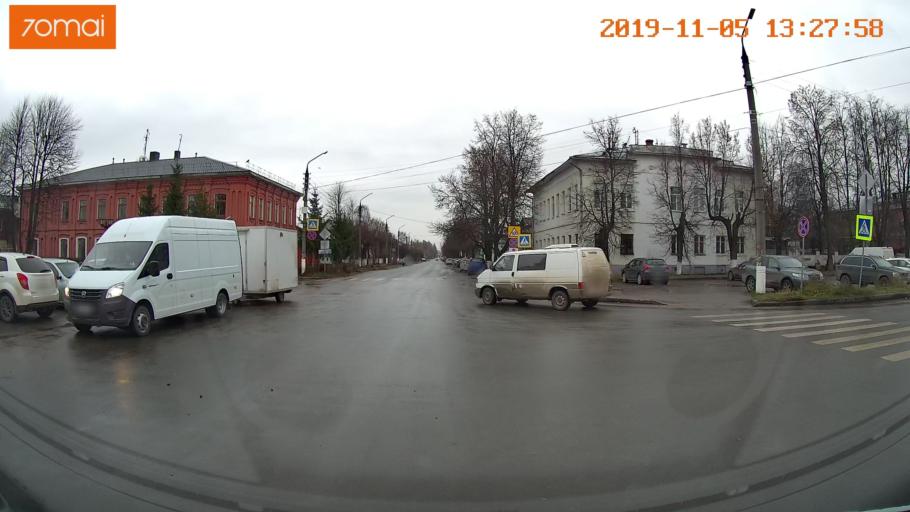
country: RU
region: Ivanovo
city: Shuya
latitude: 56.8557
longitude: 41.3840
